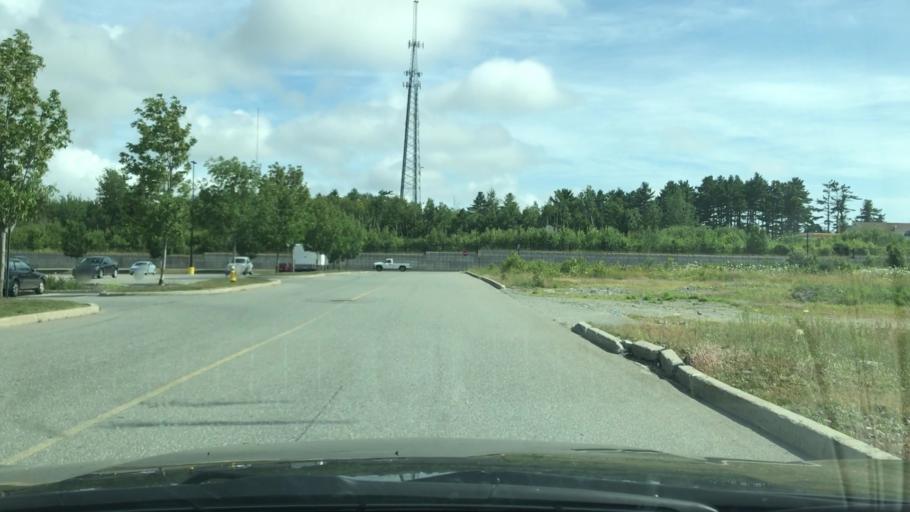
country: US
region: Maine
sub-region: Hancock County
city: Ellsworth
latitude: 44.5245
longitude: -68.3954
